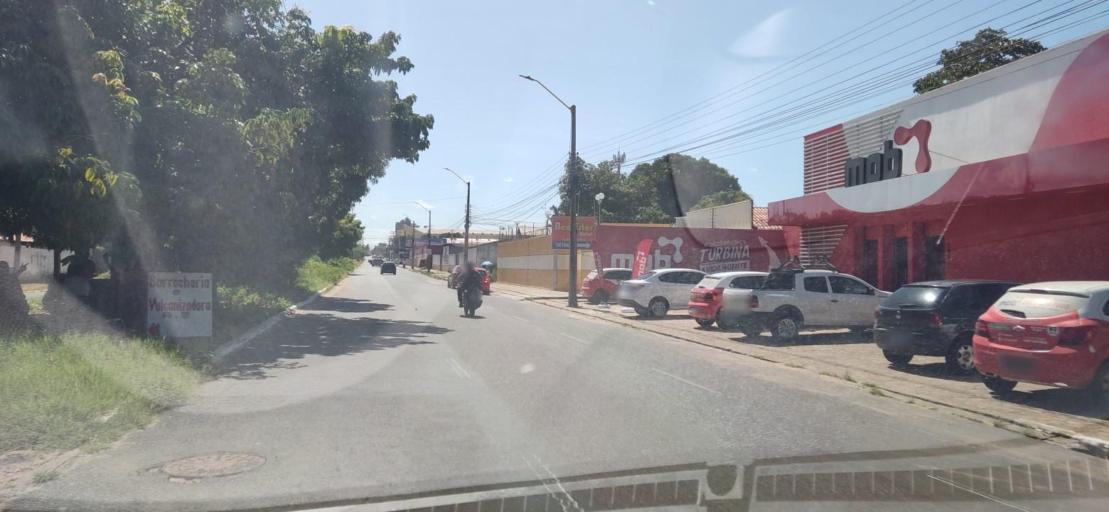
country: BR
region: Piaui
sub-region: Teresina
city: Teresina
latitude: -5.1218
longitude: -42.8073
